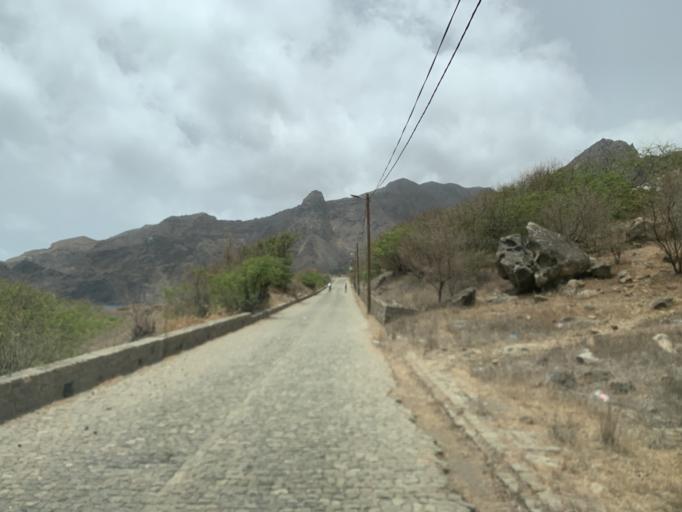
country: CV
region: Brava
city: Vila Nova Sintra
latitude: 14.8654
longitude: -24.7418
